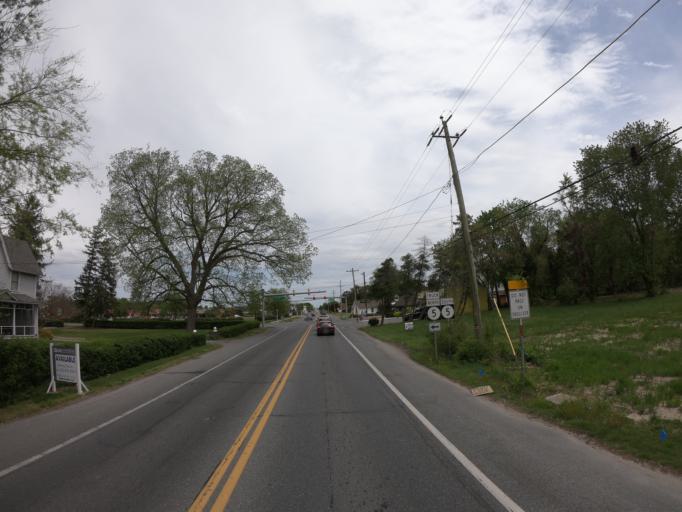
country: US
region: Delaware
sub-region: Sussex County
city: Milton
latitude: 38.7880
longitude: -75.3163
